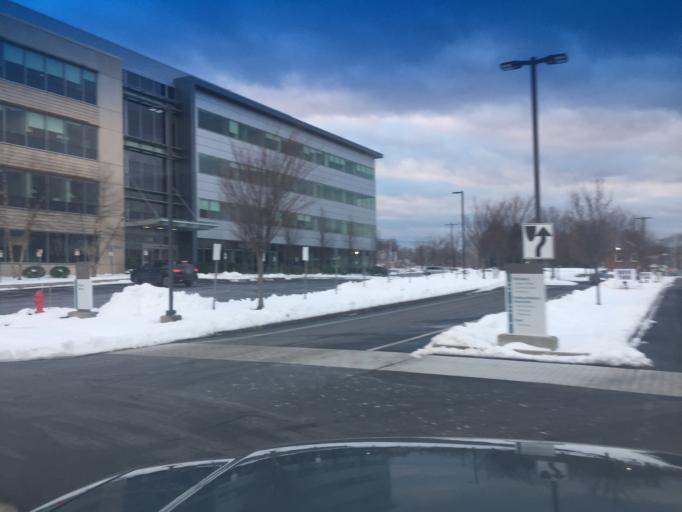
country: US
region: Massachusetts
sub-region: Norfolk County
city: Norwood
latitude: 42.1738
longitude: -71.1955
